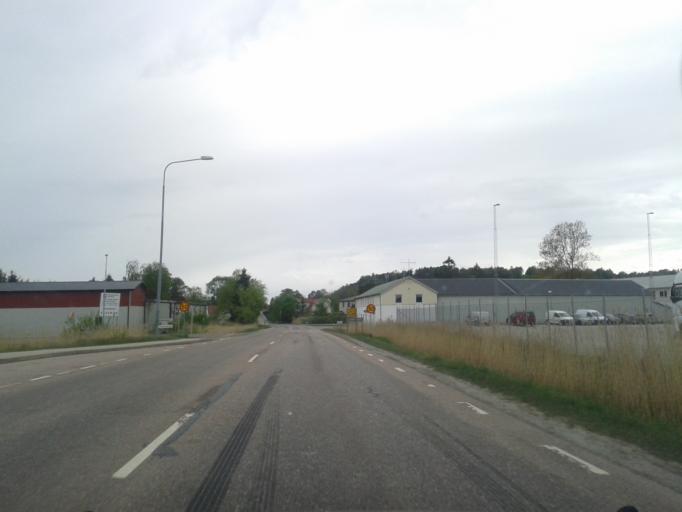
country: SE
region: Vaestra Goetaland
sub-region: Stenungsunds Kommun
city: Stora Hoga
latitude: 58.0198
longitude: 11.8401
